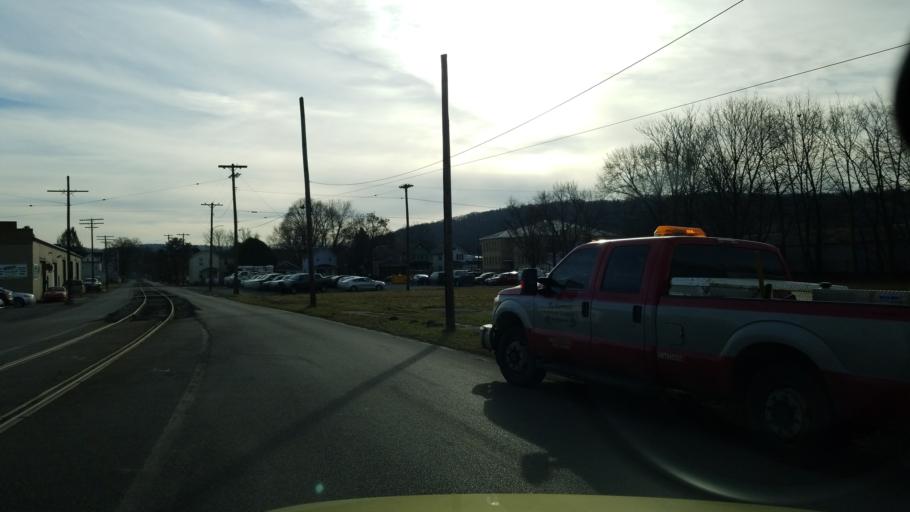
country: US
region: Pennsylvania
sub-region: Clearfield County
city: Clearfield
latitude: 41.0298
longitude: -78.4417
